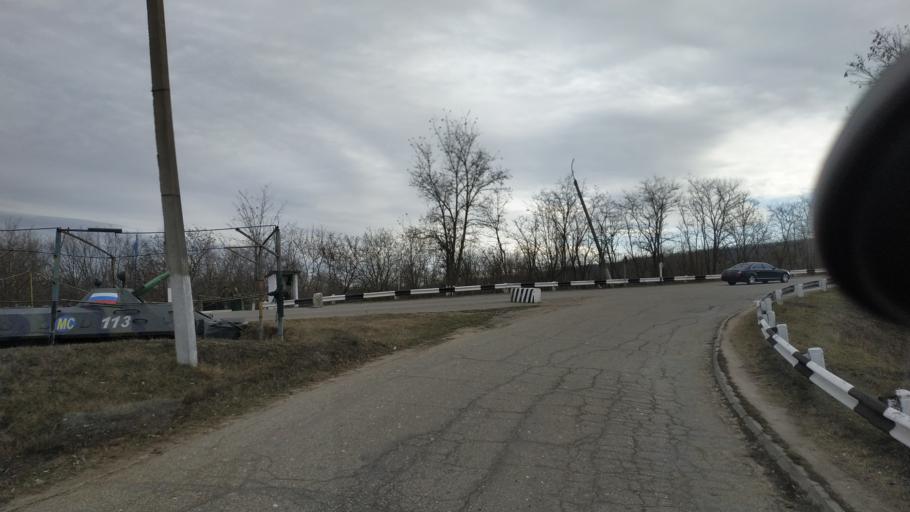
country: MD
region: Chisinau
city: Vadul lui Voda
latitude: 47.0853
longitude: 29.0886
